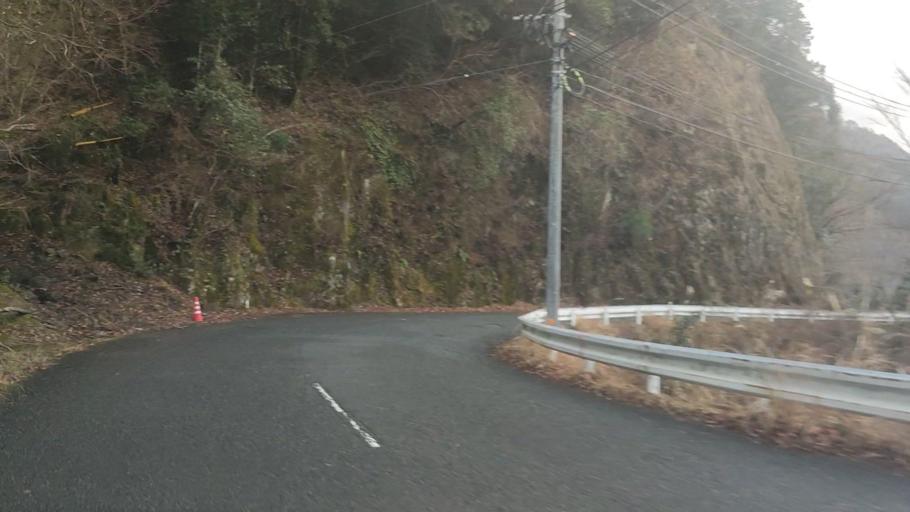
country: JP
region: Kumamoto
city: Matsubase
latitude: 32.4906
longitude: 130.9017
